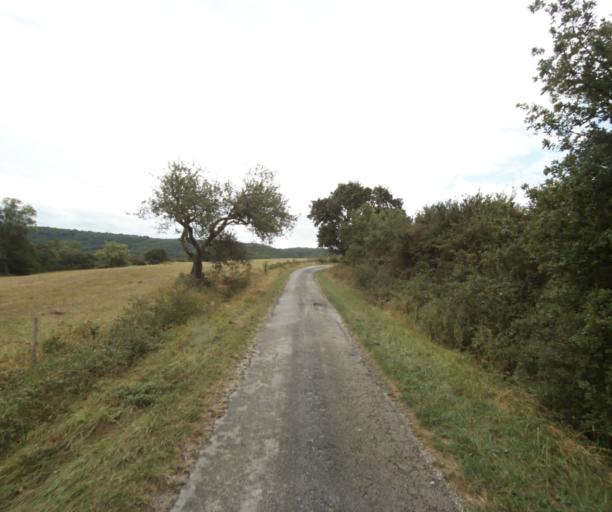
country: FR
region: Midi-Pyrenees
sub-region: Departement de la Haute-Garonne
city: Revel
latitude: 43.4216
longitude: 1.9771
